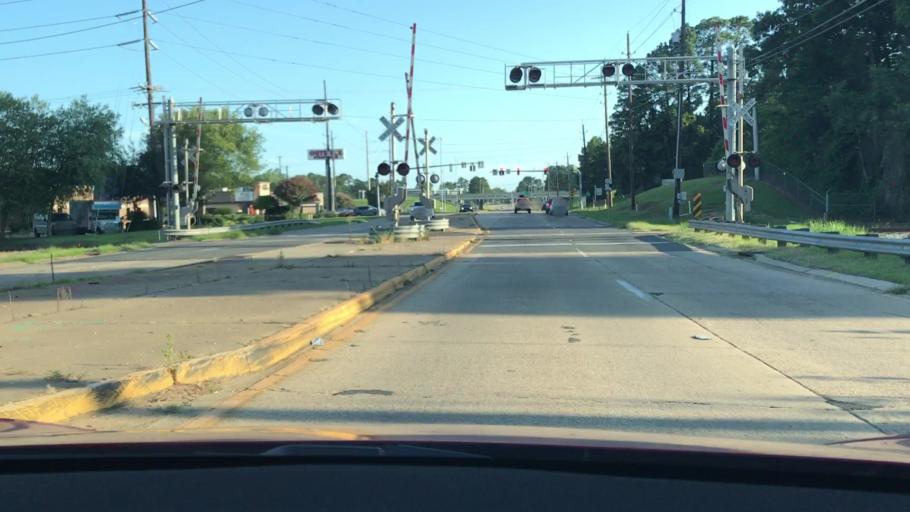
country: US
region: Louisiana
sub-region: Bossier Parish
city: Bossier City
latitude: 32.4195
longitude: -93.7362
